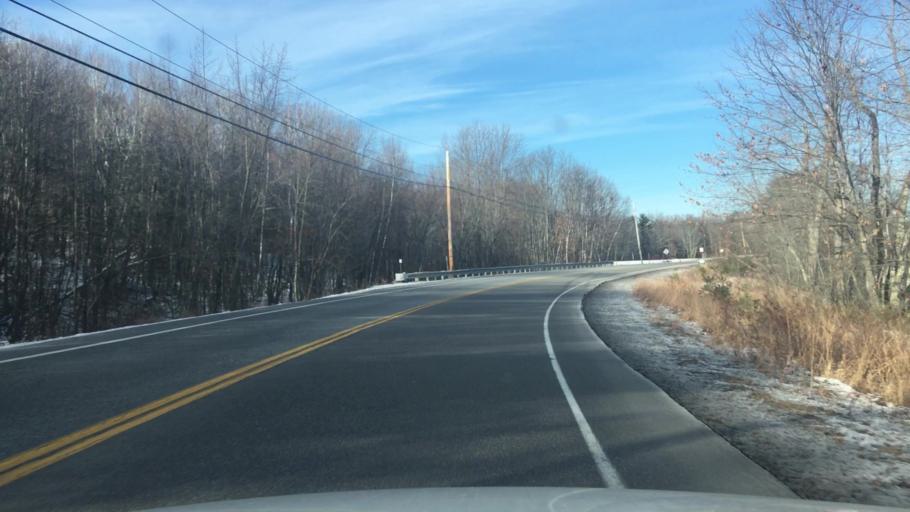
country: US
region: Maine
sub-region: Androscoggin County
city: Lisbon
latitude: 44.0090
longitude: -70.1677
